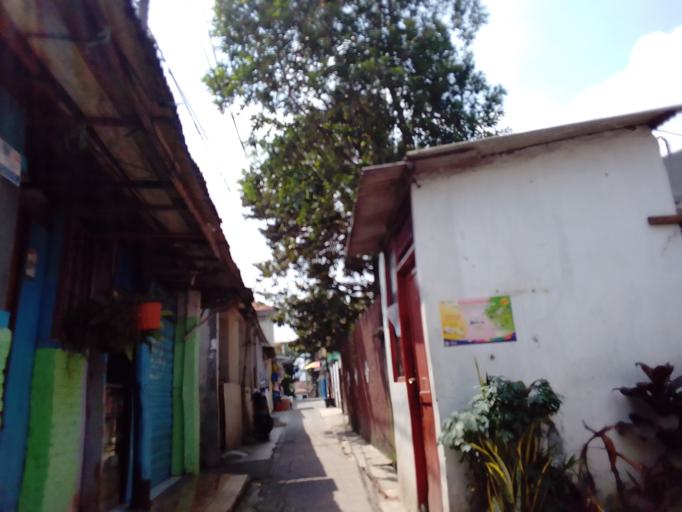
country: ID
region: Jakarta Raya
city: Jakarta
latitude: -6.2594
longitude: 106.8031
